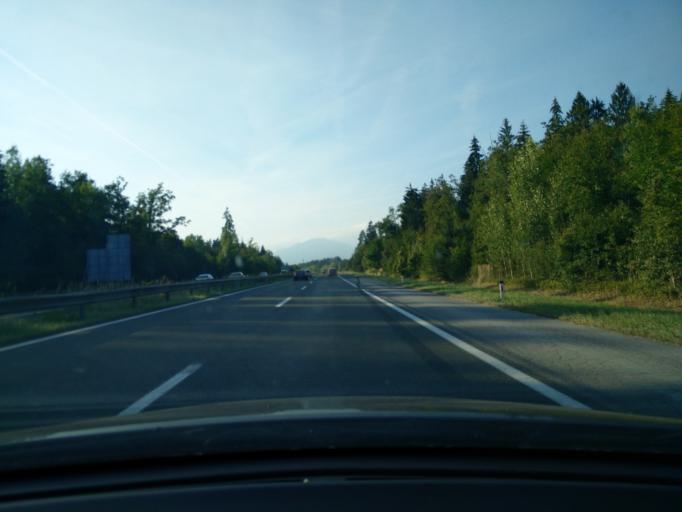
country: SI
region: Kranj
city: Britof
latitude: 46.2452
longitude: 14.3946
